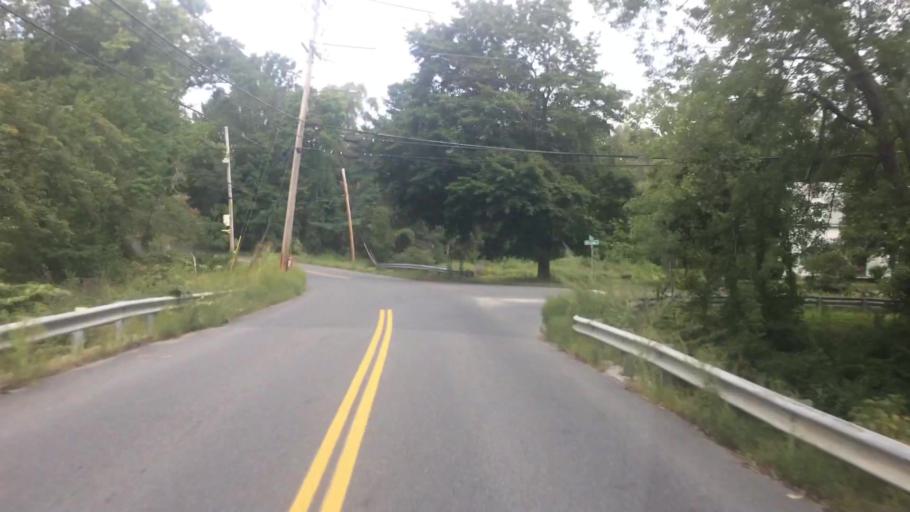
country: US
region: Massachusetts
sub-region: Middlesex County
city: Acton
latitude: 42.4637
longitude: -71.4224
